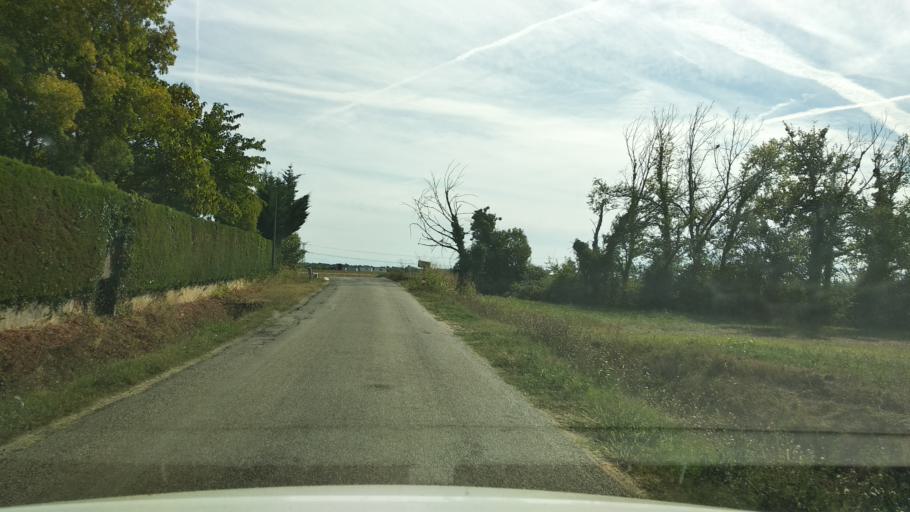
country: FR
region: Midi-Pyrenees
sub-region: Departement du Tarn-et-Garonne
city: Pompignan
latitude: 43.8103
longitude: 1.3115
